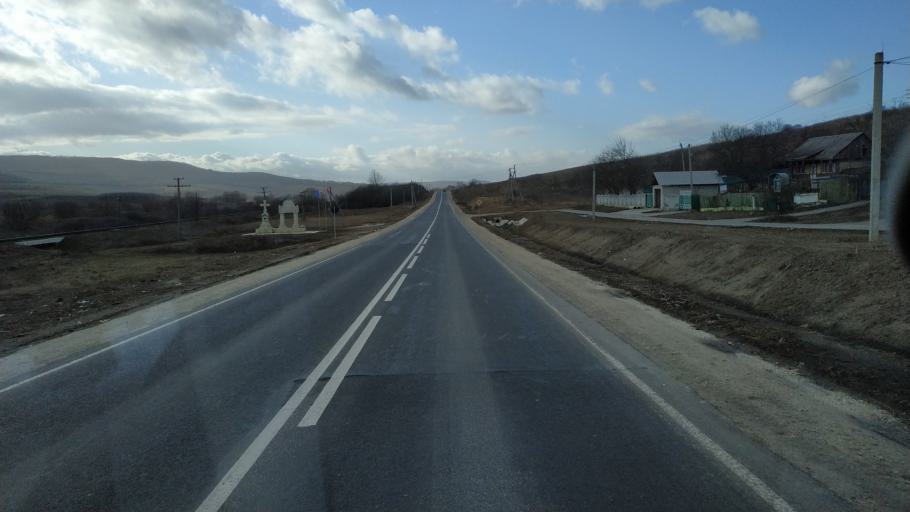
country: MD
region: Calarasi
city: Calarasi
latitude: 47.2907
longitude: 28.1831
